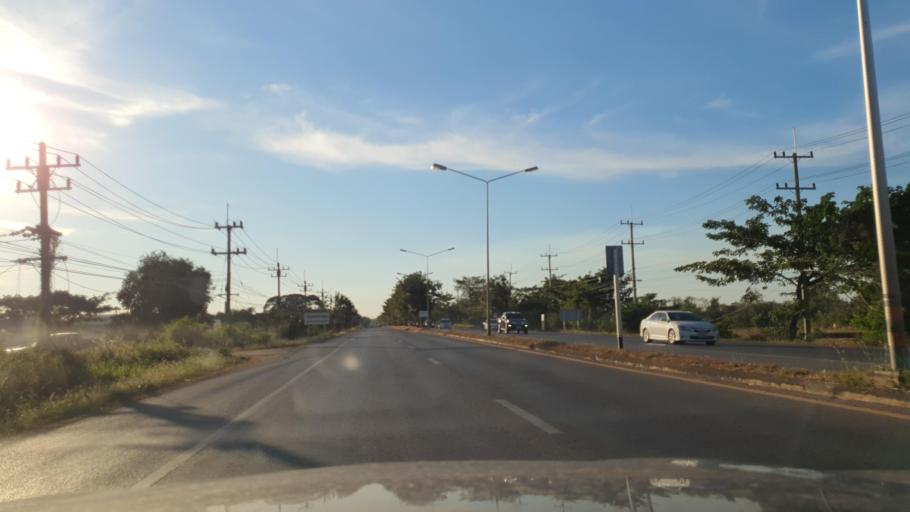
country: TH
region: Khon Kaen
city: Khon Kaen
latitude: 16.4375
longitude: 102.9115
